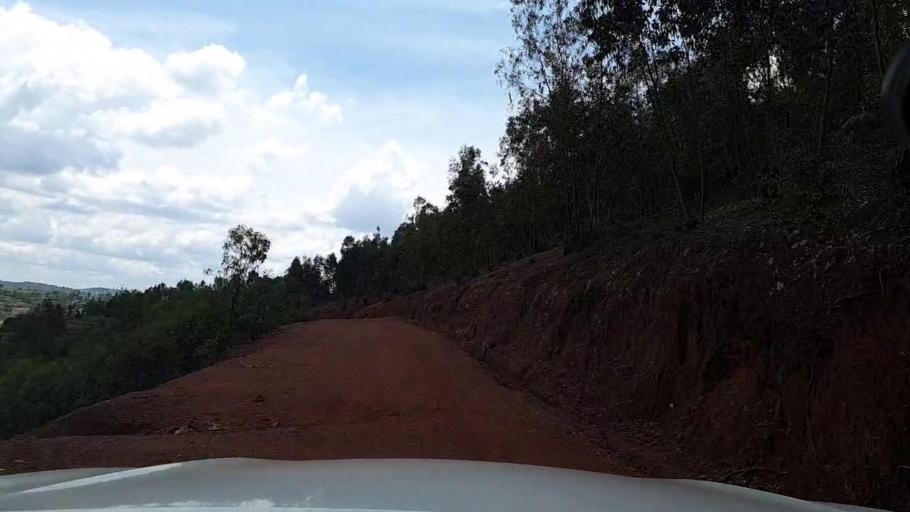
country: RW
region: Southern Province
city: Butare
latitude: -2.7548
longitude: 29.7497
